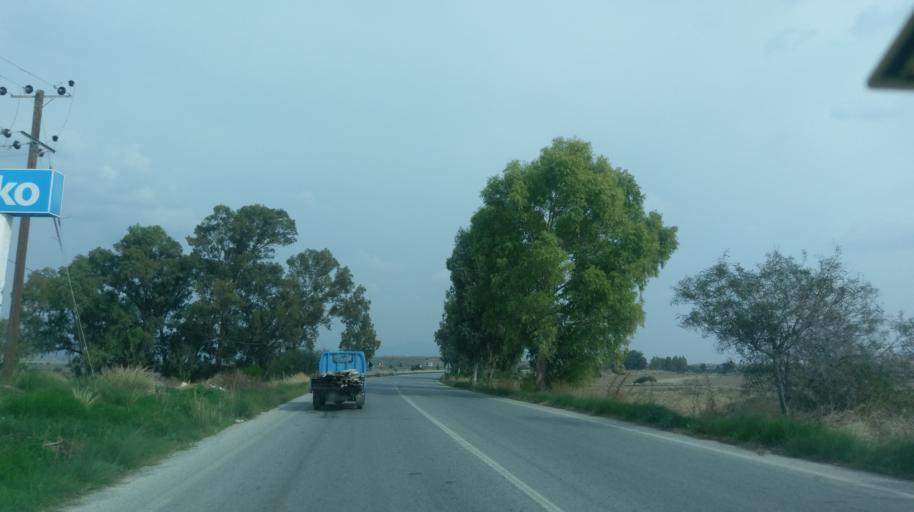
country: CY
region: Ammochostos
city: Lefkonoiko
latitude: 35.2478
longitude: 33.6119
